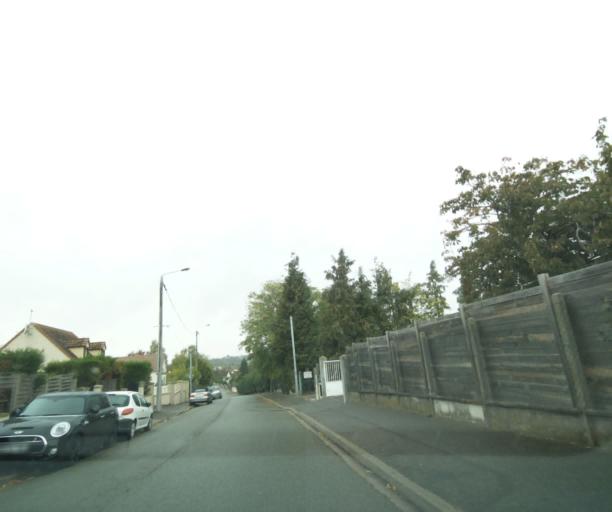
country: FR
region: Centre
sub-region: Departement d'Eure-et-Loir
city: Luray
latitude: 48.7333
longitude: 1.3856
